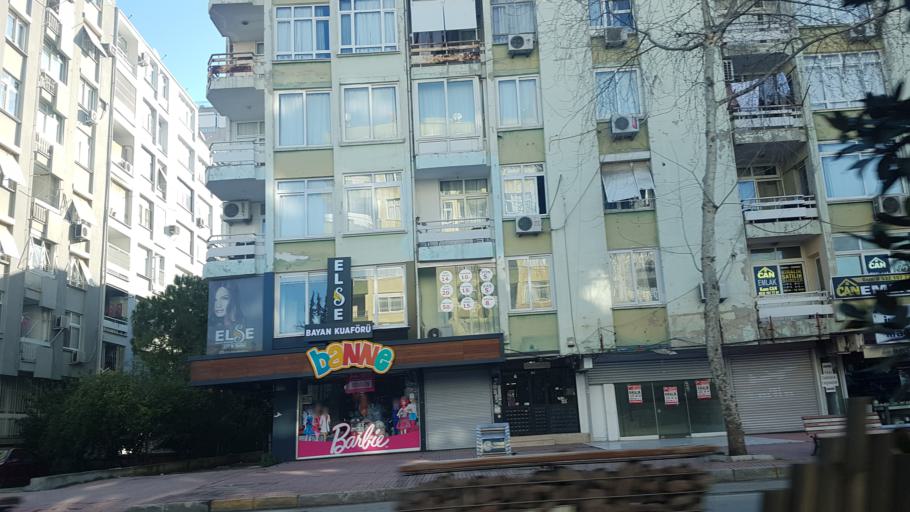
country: TR
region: Adana
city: Adana
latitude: 37.0197
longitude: 35.3162
